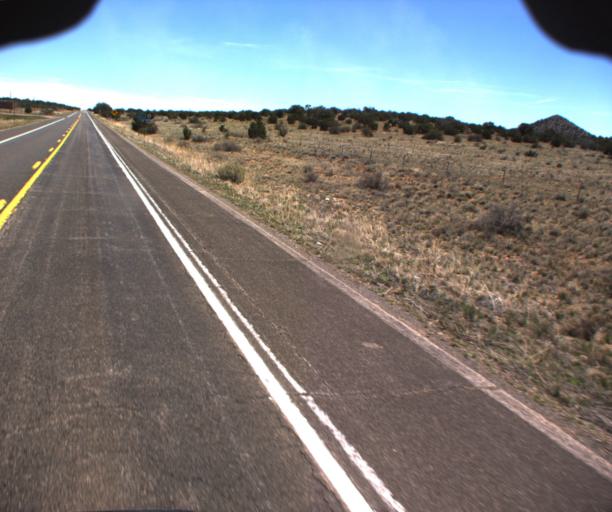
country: US
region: Arizona
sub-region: Mohave County
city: Peach Springs
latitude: 35.5525
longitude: -113.3143
